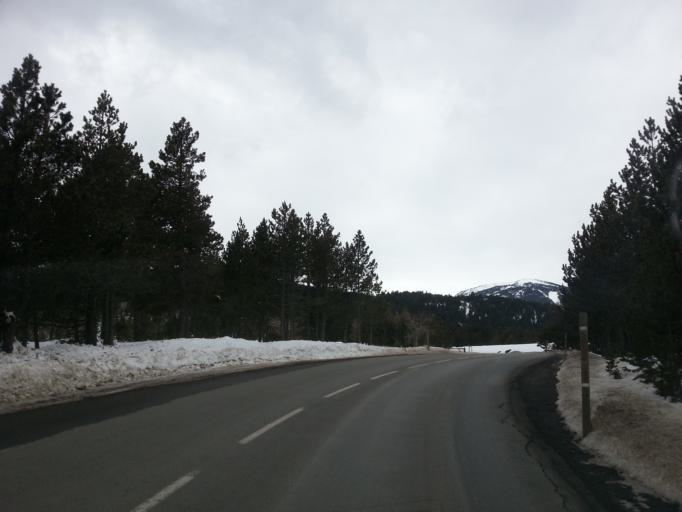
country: ES
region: Catalonia
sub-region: Provincia de Girona
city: Llivia
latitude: 42.5445
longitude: 2.0927
